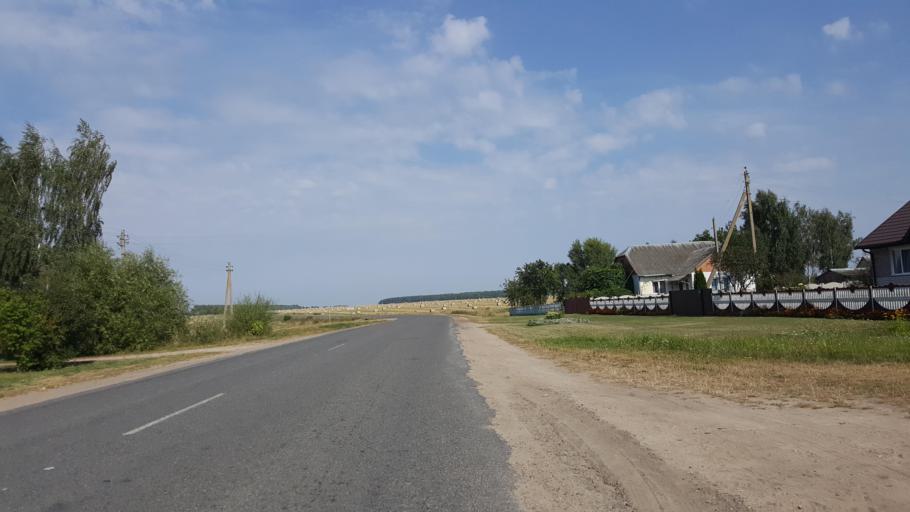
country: BY
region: Brest
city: Kamyanyets
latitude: 52.4327
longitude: 23.7489
